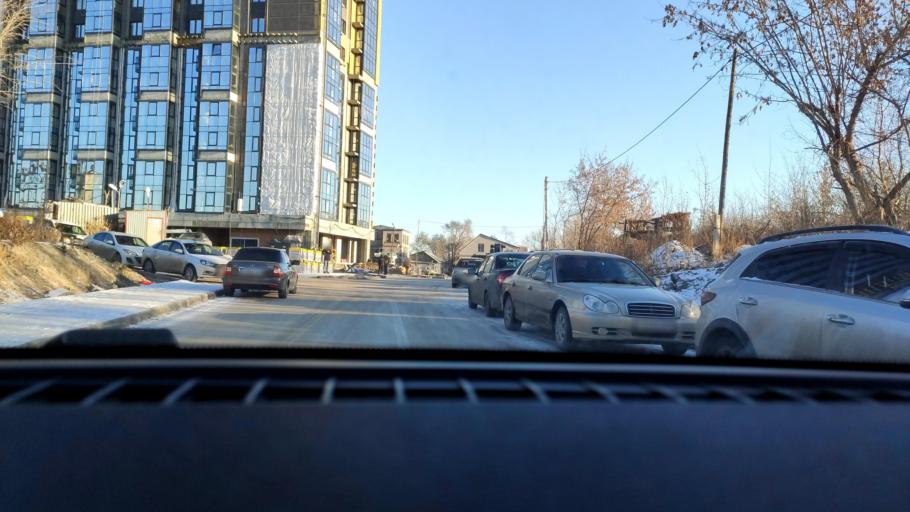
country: RU
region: Samara
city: Samara
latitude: 53.2176
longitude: 50.1376
